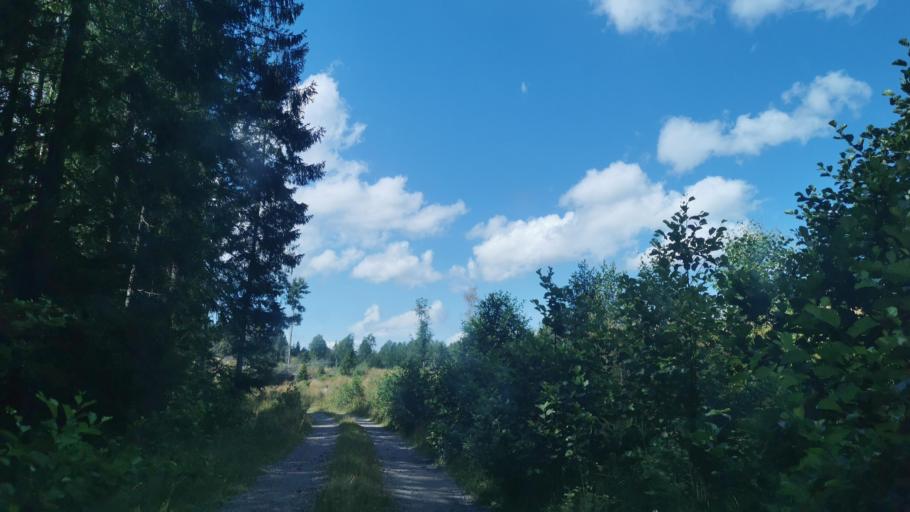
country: SE
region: OEstergoetland
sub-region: Finspangs Kommun
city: Finspang
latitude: 58.8009
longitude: 15.8100
